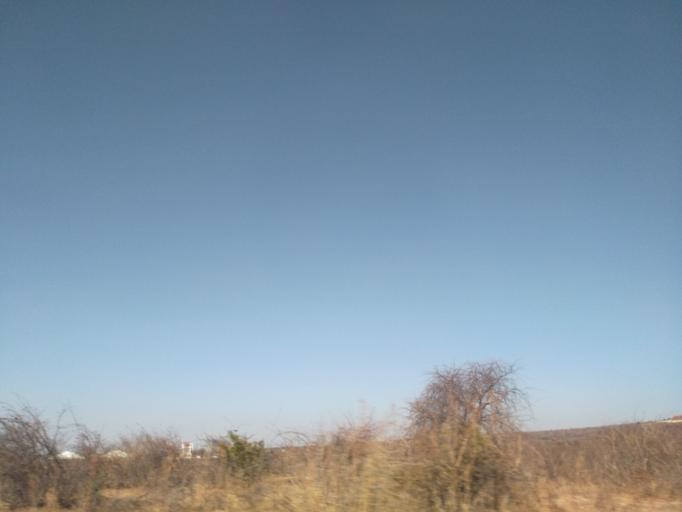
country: TZ
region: Dodoma
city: Dodoma
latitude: -6.1726
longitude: 35.7011
